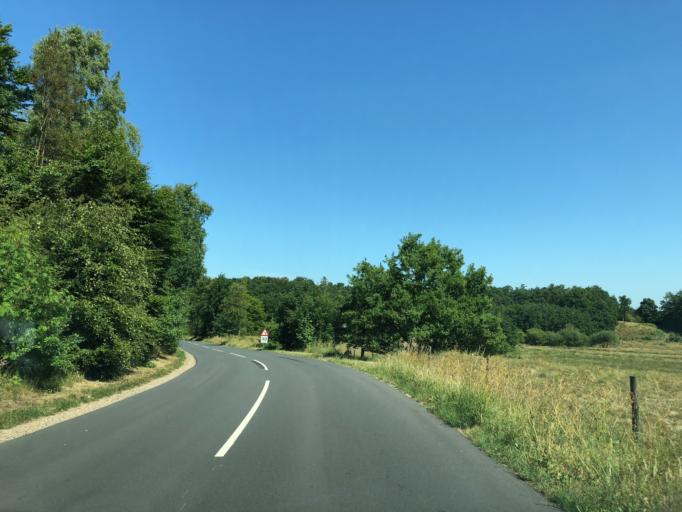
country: DK
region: Central Jutland
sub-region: Holstebro Kommune
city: Holstebro
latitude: 56.3483
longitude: 8.6879
